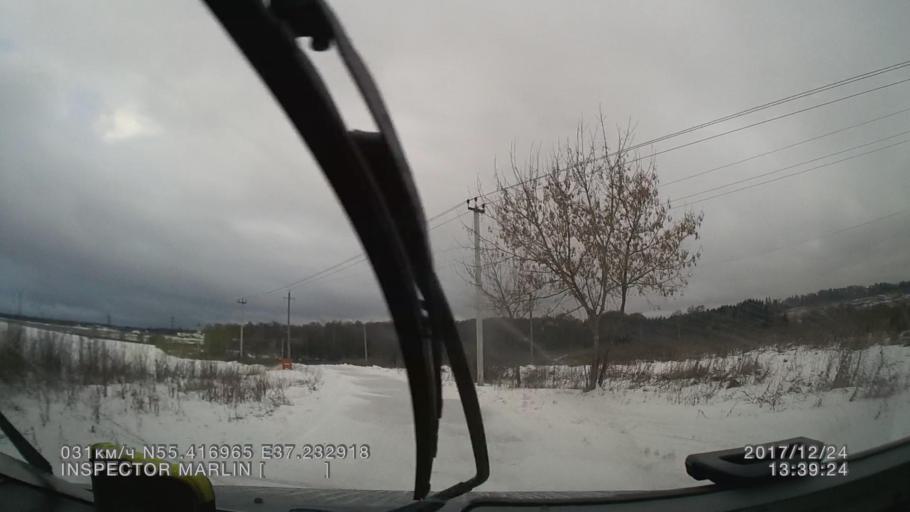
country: RU
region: Moskovskaya
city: Troitsk
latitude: 55.4170
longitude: 37.2329
